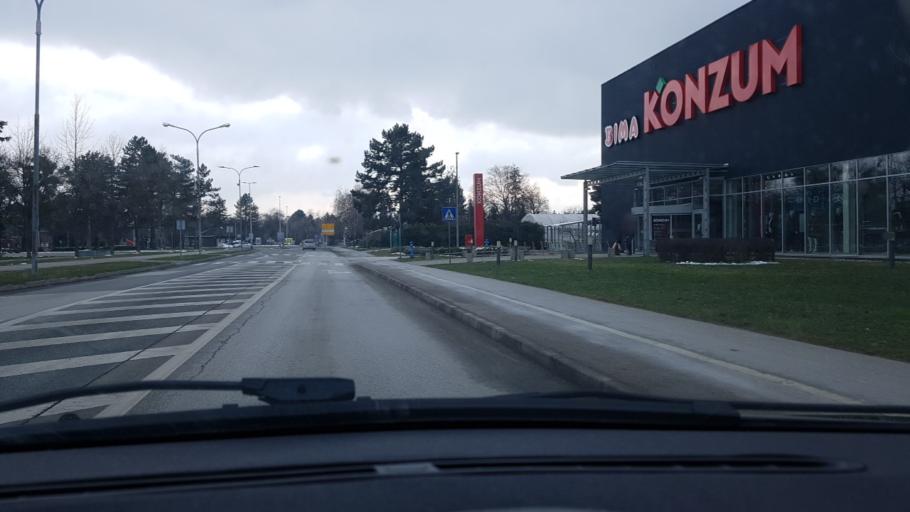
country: HR
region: Varazdinska
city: Varazdin
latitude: 46.3117
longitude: 16.3269
